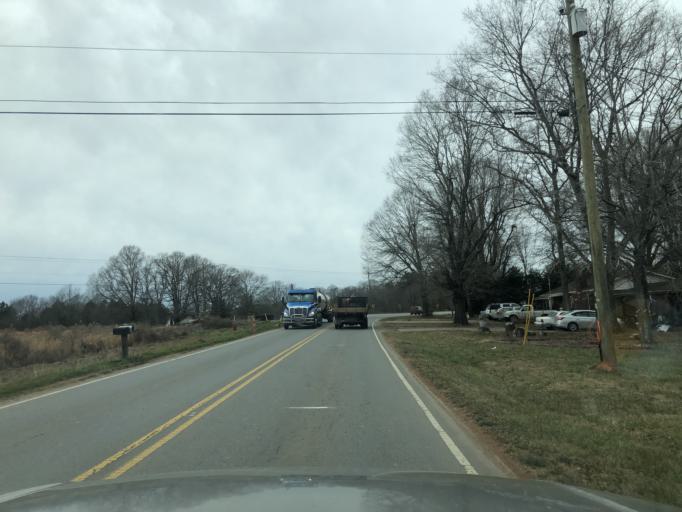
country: US
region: North Carolina
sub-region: Cleveland County
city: Shelby
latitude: 35.3139
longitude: -81.4927
